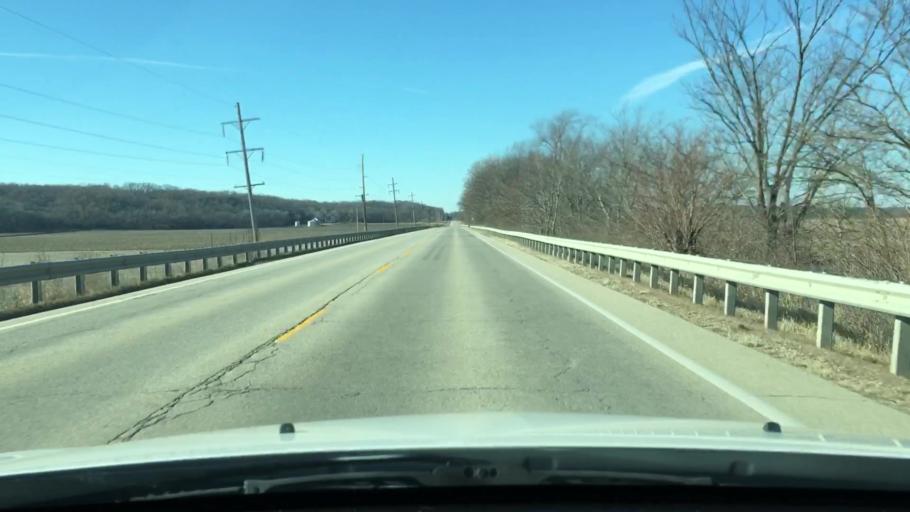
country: US
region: Illinois
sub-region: Mason County
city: Havana
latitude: 40.3024
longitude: -90.1216
